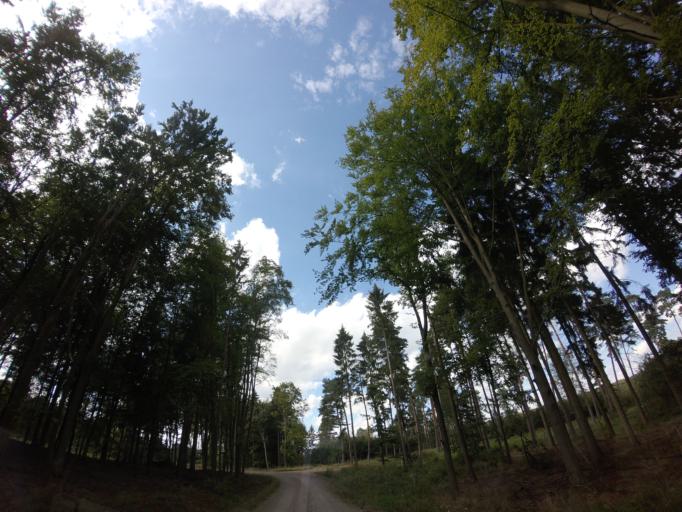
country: PL
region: West Pomeranian Voivodeship
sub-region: Powiat choszczenski
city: Recz
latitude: 53.2944
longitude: 15.6200
